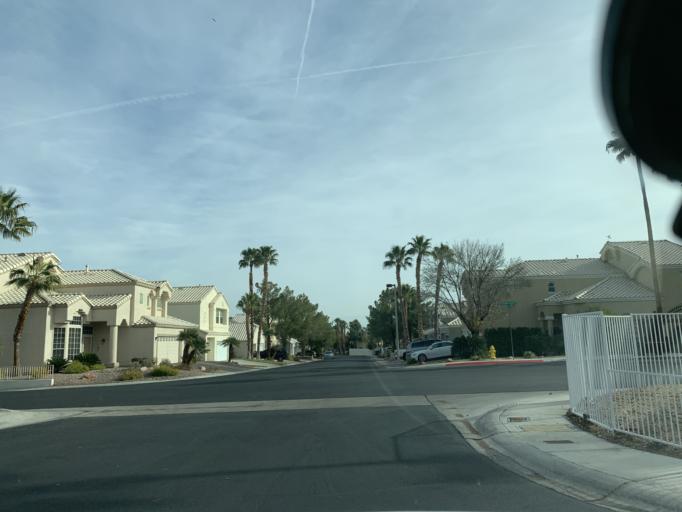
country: US
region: Nevada
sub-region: Clark County
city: Summerlin South
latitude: 36.1542
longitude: -115.2993
